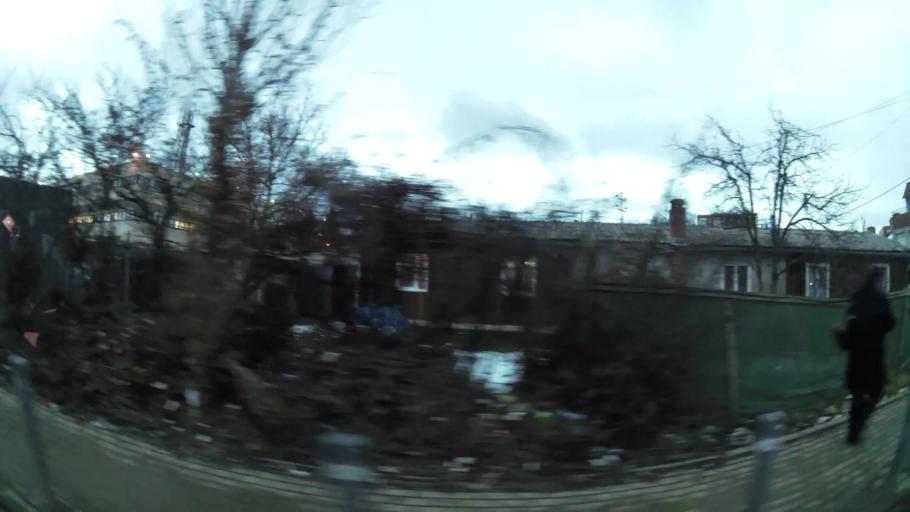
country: XK
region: Pristina
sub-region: Komuna e Prishtines
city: Pristina
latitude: 42.6447
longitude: 21.1672
